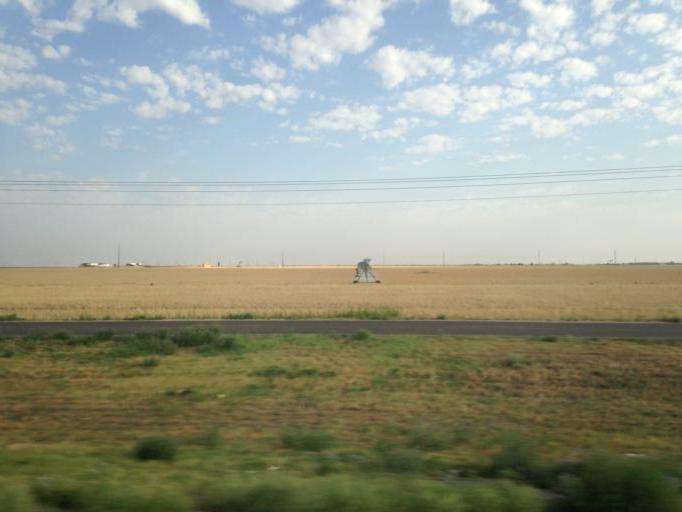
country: US
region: Texas
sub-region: Martin County
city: Stanton
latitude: 32.1094
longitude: -101.8444
